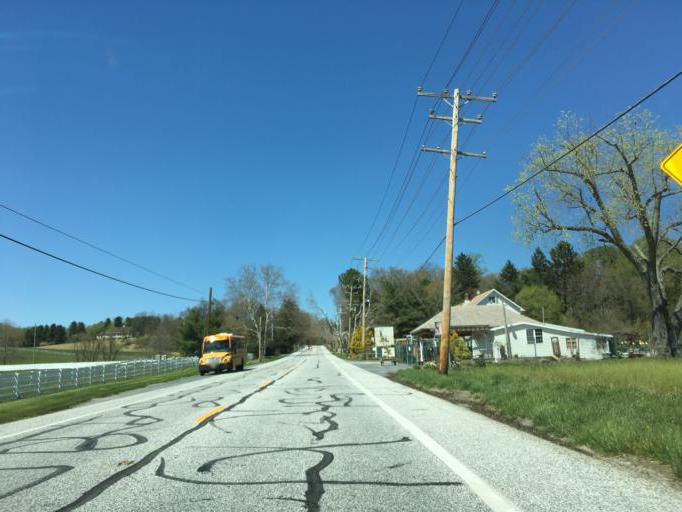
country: US
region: Maryland
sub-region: Baltimore County
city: Hunt Valley
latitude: 39.5758
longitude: -76.6604
